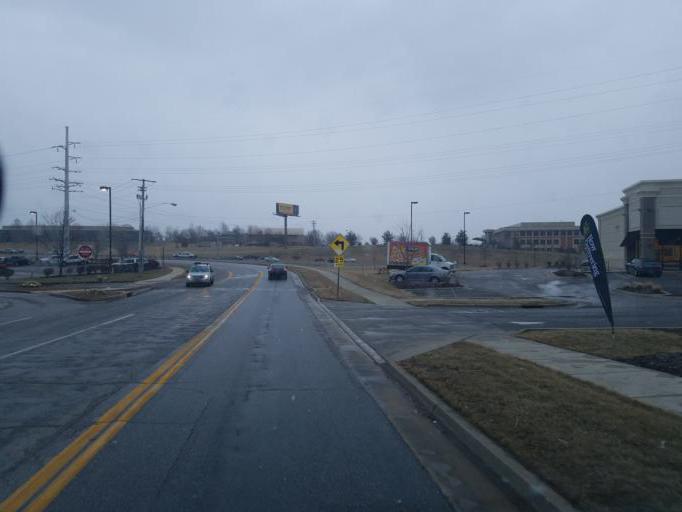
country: US
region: Missouri
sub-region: Boone County
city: Columbia
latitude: 38.9485
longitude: -92.2952
